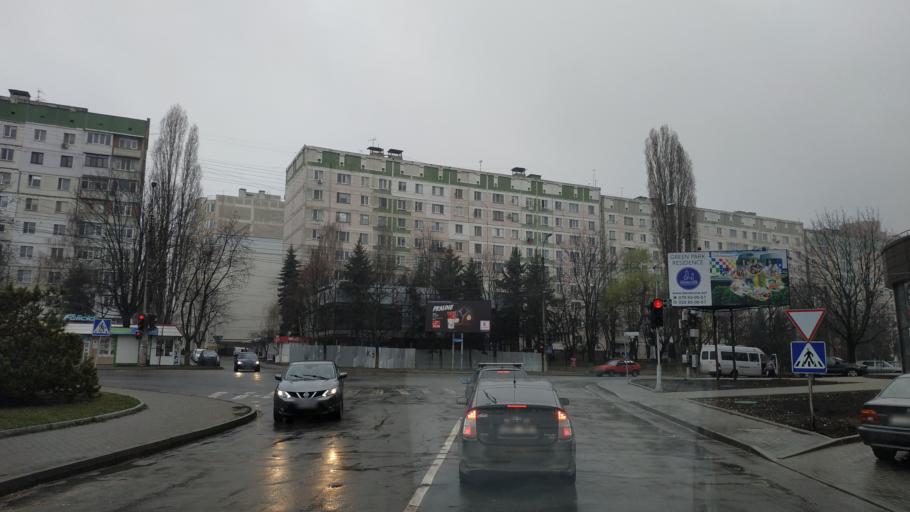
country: MD
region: Chisinau
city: Vatra
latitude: 47.0430
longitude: 28.7708
